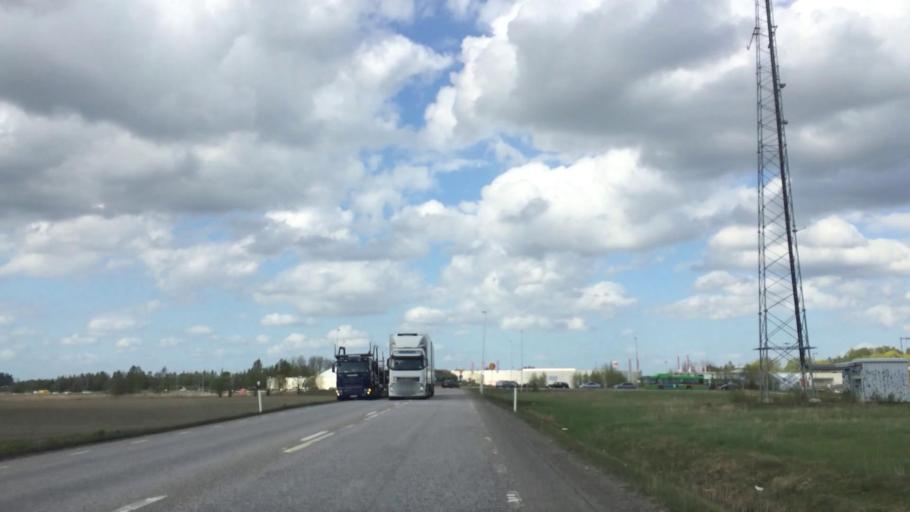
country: SE
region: Soedermanland
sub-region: Eskilstuna Kommun
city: Eskilstuna
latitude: 59.3706
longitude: 16.4641
